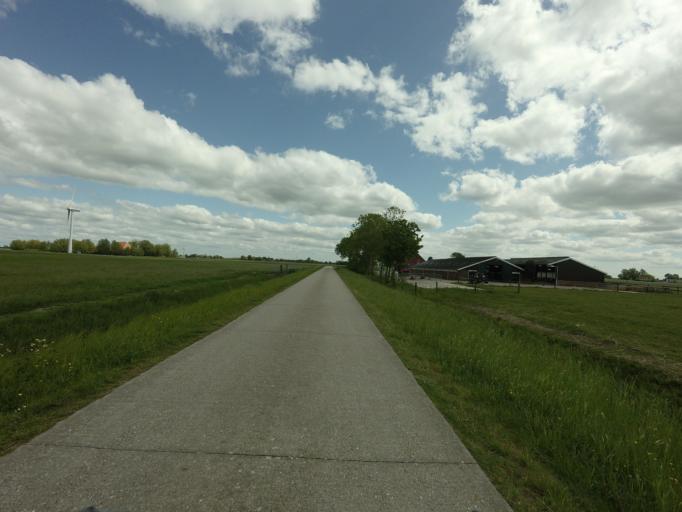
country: NL
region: Friesland
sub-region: Gemeente Franekeradeel
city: Tzum
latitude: 53.1265
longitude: 5.5521
